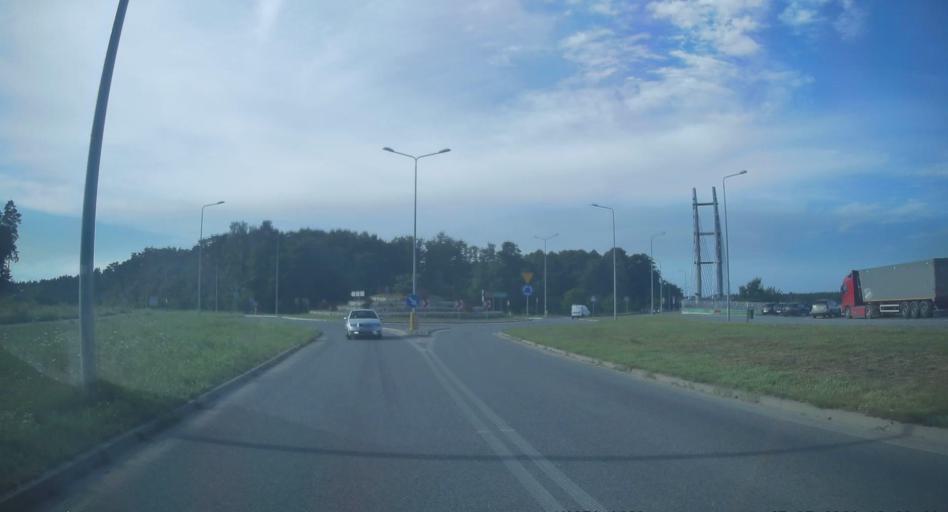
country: PL
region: Swietokrzyskie
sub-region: Powiat konecki
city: Smykow
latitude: 51.1098
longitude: 20.3481
